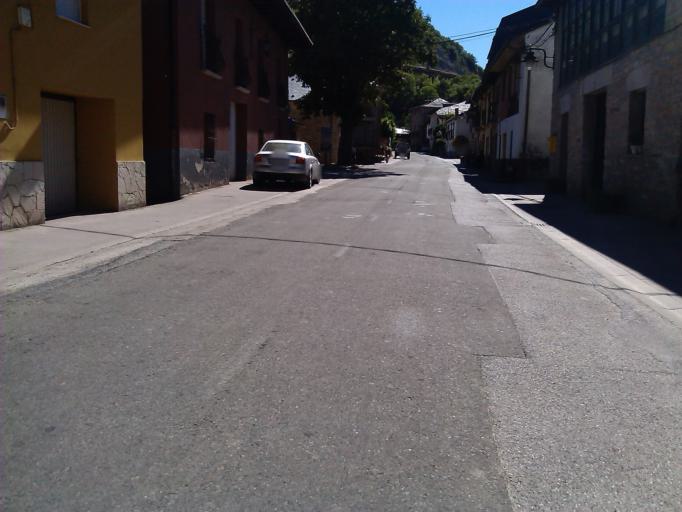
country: ES
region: Castille and Leon
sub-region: Provincia de Leon
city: Vega de Valcarce
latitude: 42.6657
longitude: -6.9287
